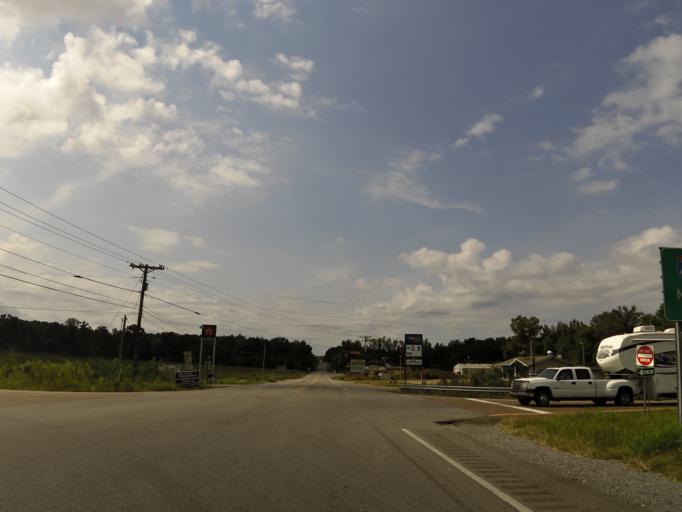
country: US
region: Tennessee
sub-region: Humphreys County
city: Waverly
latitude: 35.8790
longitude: -87.8022
